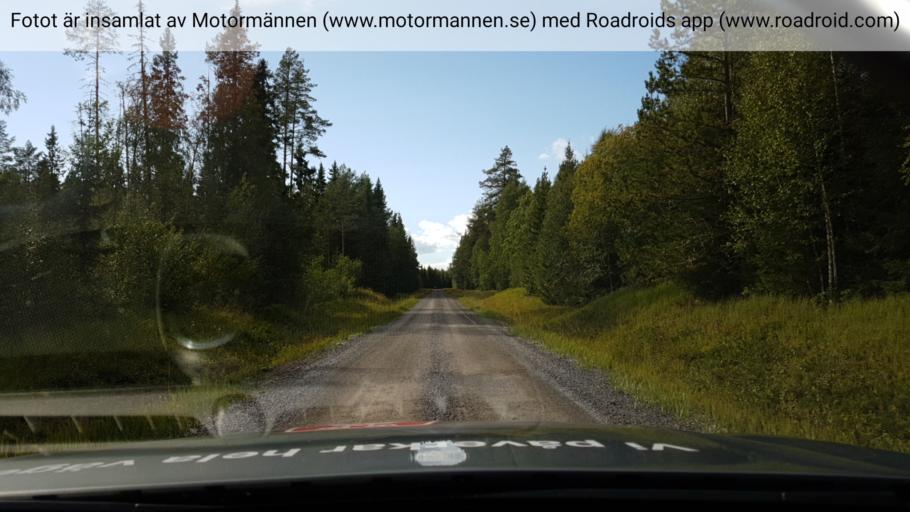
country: SE
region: Jaemtland
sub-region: OEstersunds Kommun
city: Lit
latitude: 63.3079
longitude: 15.2546
